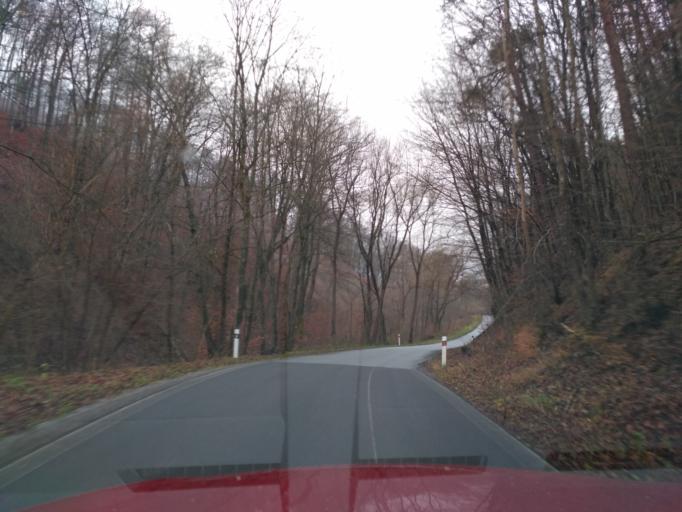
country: SK
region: Presovsky
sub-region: Okres Presov
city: Presov
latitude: 48.8979
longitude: 21.1966
